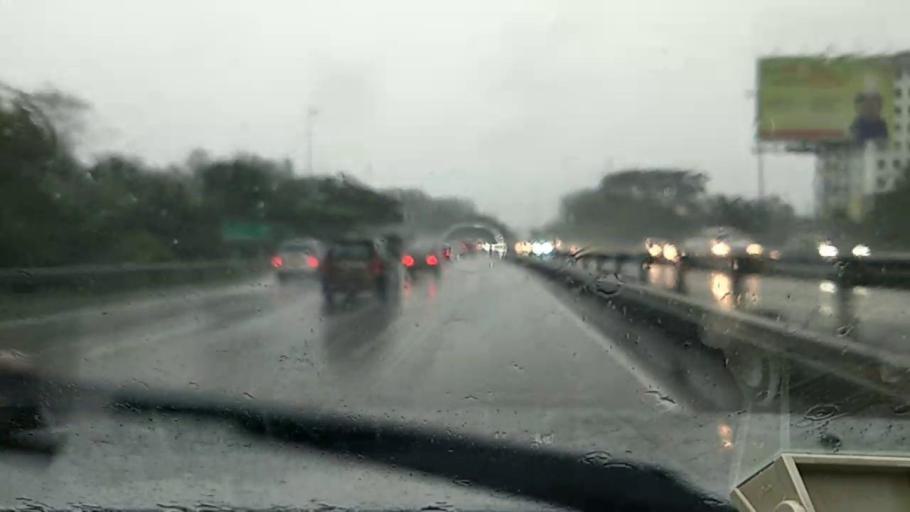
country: MY
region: Putrajaya
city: Putrajaya
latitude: 2.9773
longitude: 101.7263
